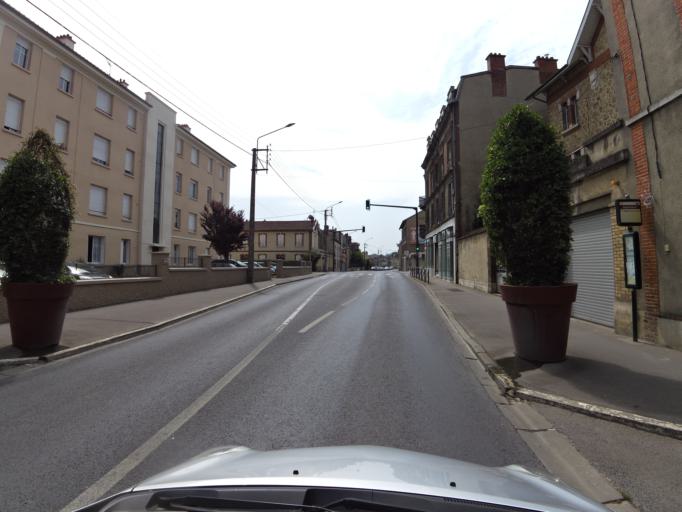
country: FR
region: Champagne-Ardenne
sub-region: Departement de la Marne
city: Epernay
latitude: 49.0373
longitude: 3.9489
